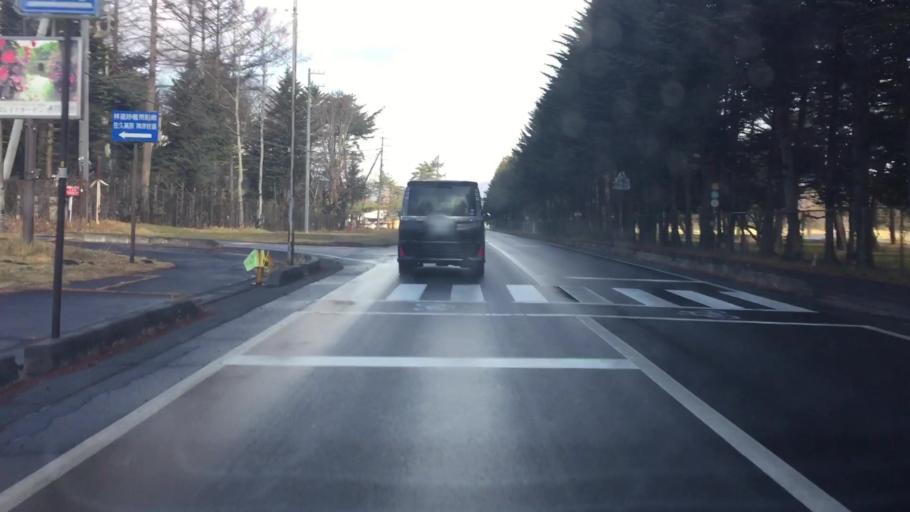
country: JP
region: Nagano
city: Saku
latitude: 36.3076
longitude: 138.6317
